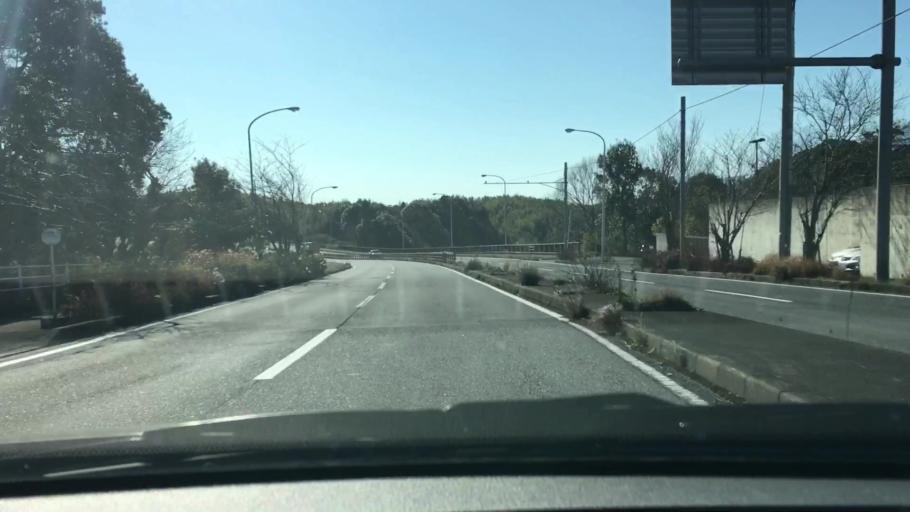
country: JP
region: Chiba
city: Narita
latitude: 35.7400
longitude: 140.4014
